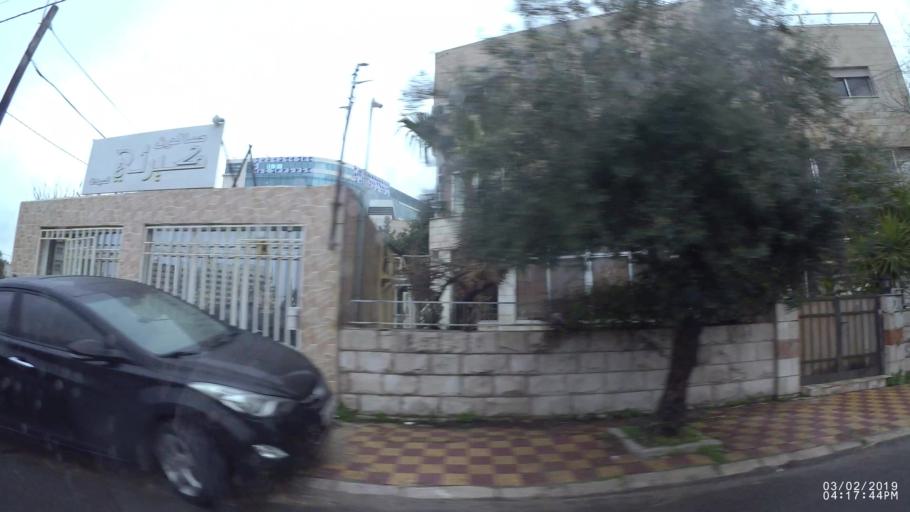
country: JO
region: Amman
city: Amman
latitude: 31.9681
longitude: 35.9122
